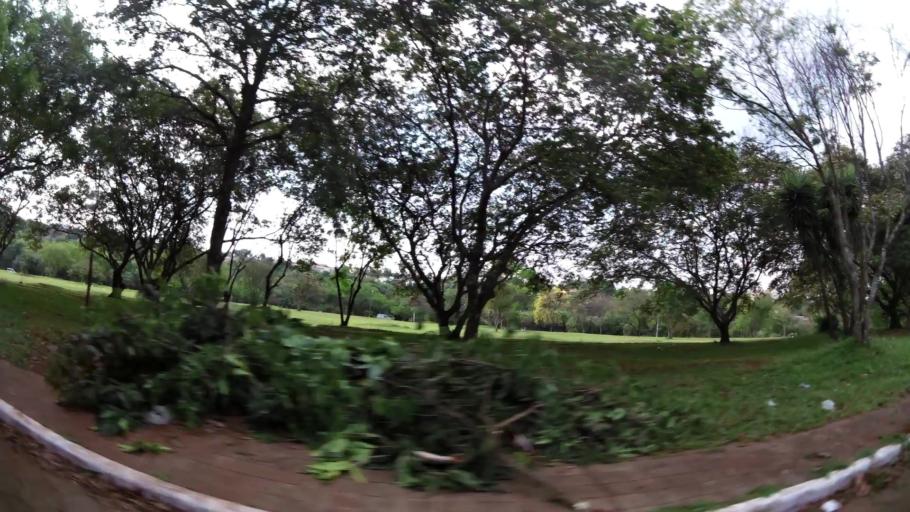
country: PY
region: Alto Parana
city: Presidente Franco
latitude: -25.5249
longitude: -54.6333
